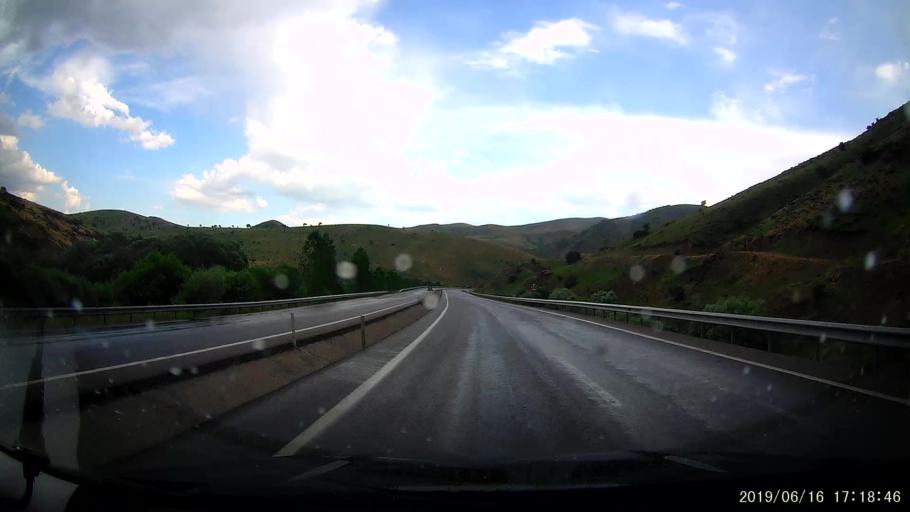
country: TR
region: Erzincan
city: Tercan
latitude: 39.8093
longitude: 40.5297
